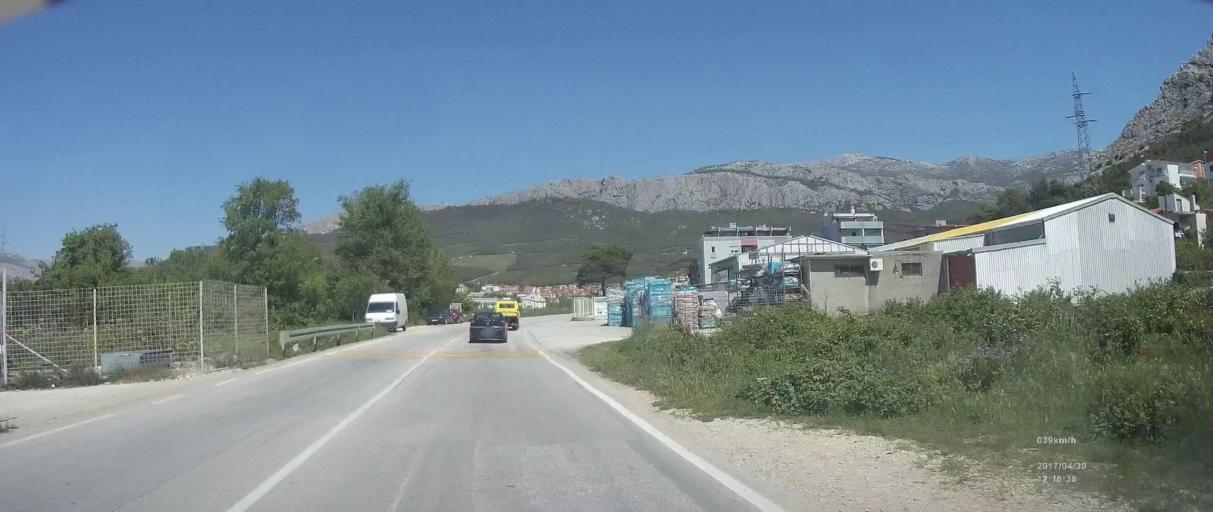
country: HR
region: Splitsko-Dalmatinska
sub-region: Grad Split
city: Stobrec
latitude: 43.5117
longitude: 16.5393
